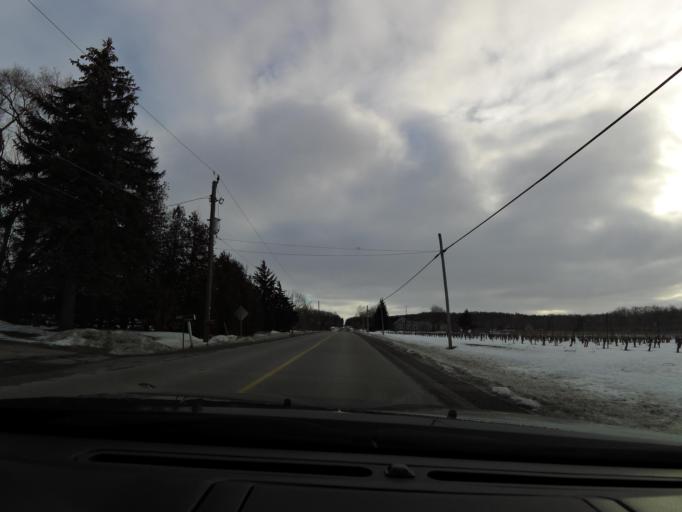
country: CA
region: Ontario
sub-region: Regional Municipality of Niagara
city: St. Catharines
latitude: 43.1718
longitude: -79.4973
